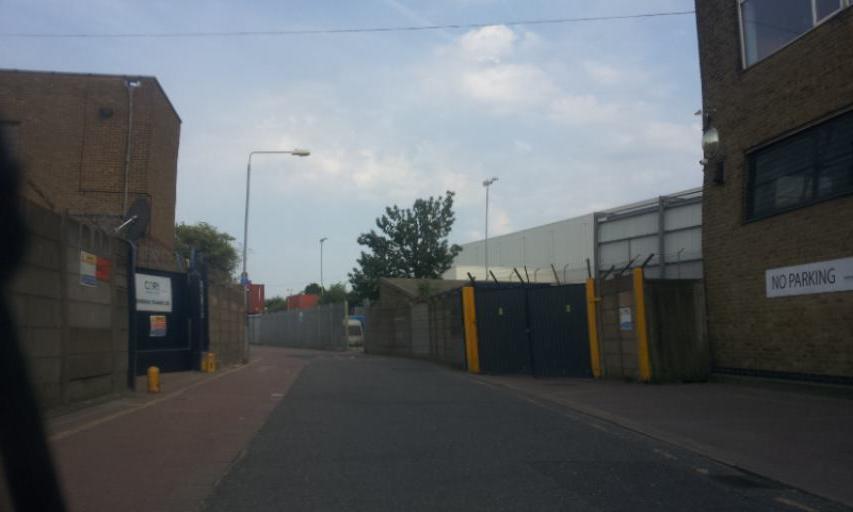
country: GB
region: England
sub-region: Greater London
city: Blackheath
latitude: 51.4934
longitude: 0.0262
